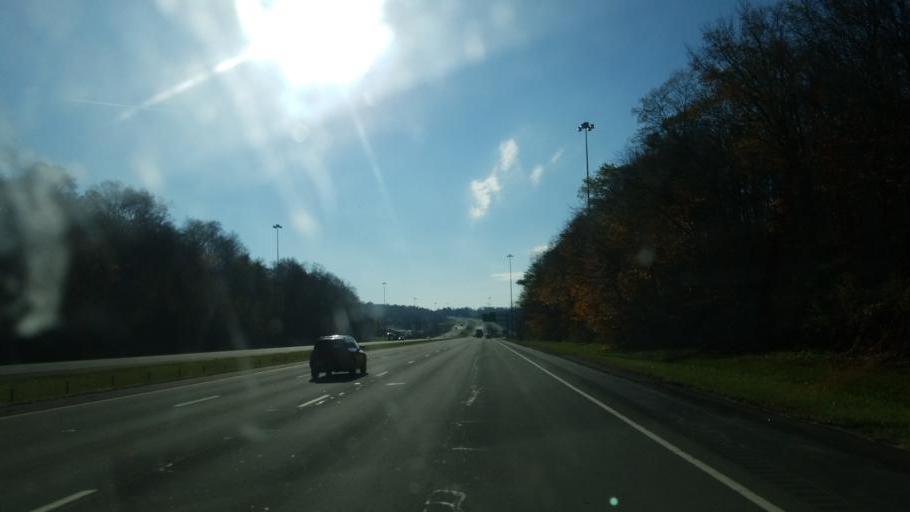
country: US
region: Ohio
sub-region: Richland County
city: Mansfield
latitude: 40.7006
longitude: -82.5020
